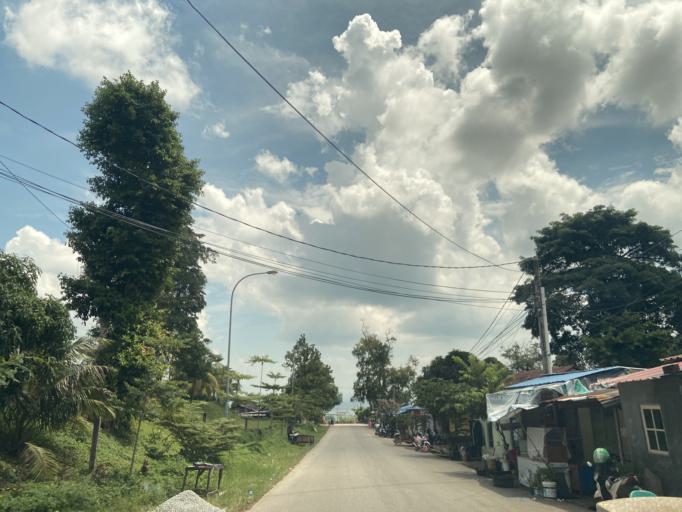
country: SG
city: Singapore
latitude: 1.1577
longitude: 104.0118
